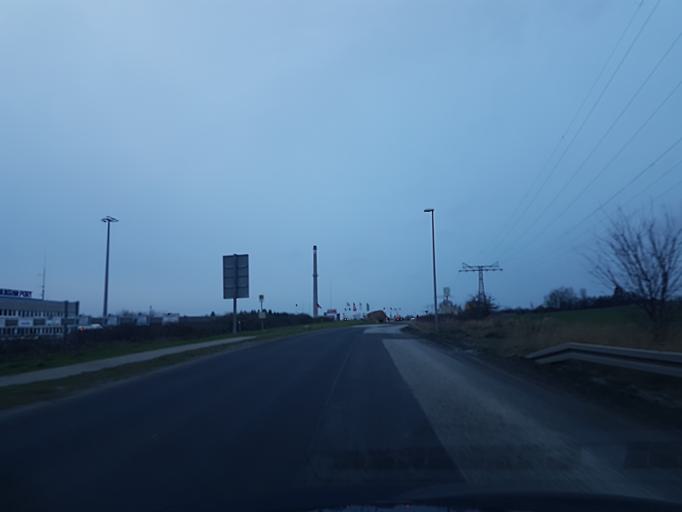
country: DE
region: Mecklenburg-Vorpommern
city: Sagard
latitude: 54.4912
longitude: 13.5823
